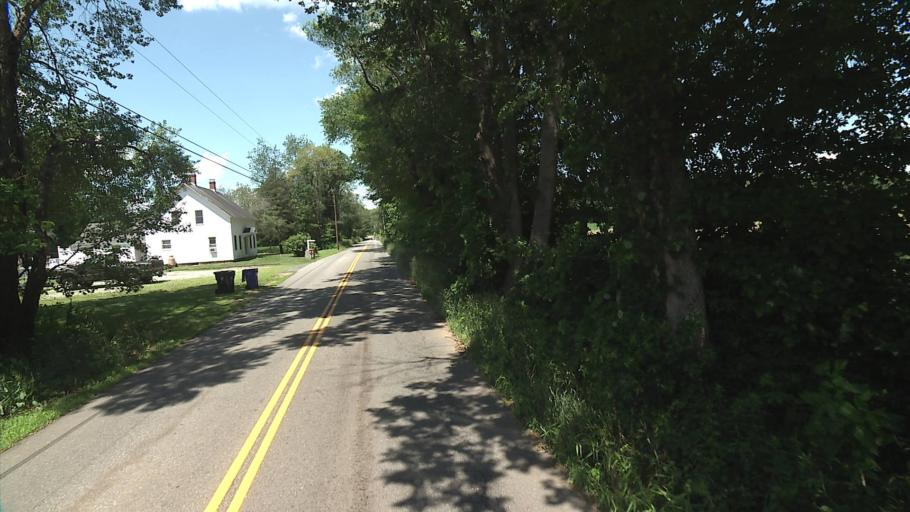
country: US
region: Connecticut
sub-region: New London County
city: Jewett City
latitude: 41.6106
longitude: -71.9308
